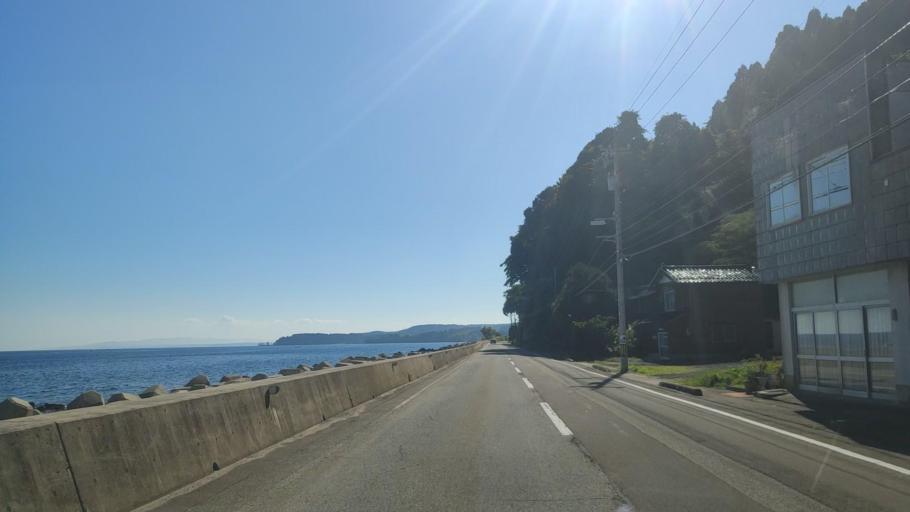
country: JP
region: Ishikawa
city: Nanao
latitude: 37.2827
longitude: 137.1093
